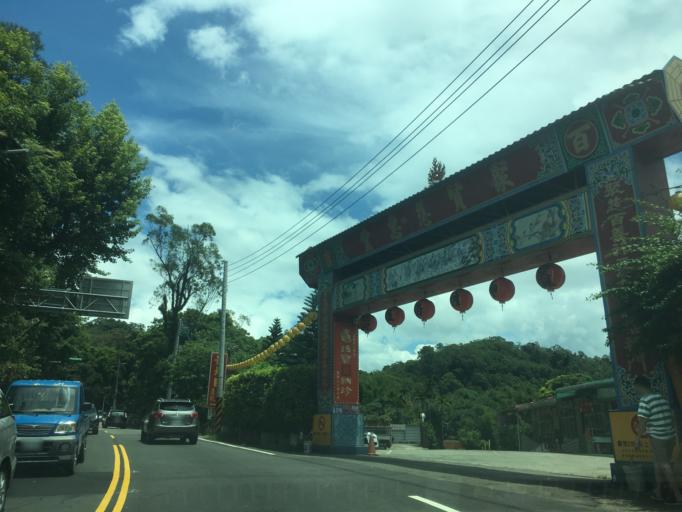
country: TW
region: Taiwan
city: Daxi
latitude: 24.8257
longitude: 121.3113
